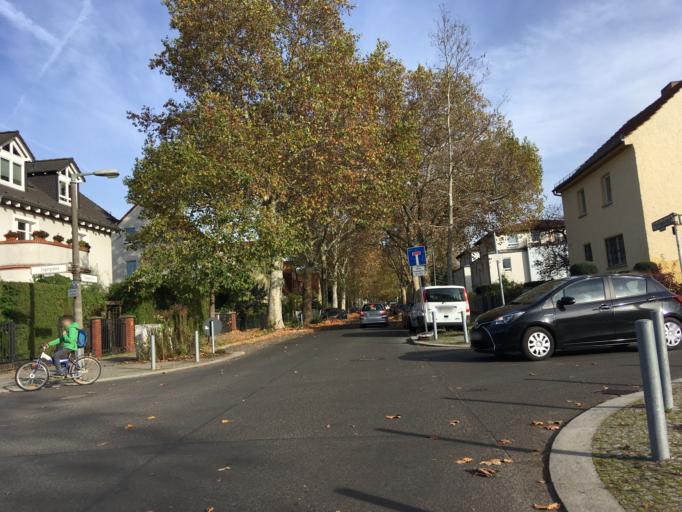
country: DE
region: Berlin
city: Wilhelmsruh
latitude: 52.5831
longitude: 13.3852
